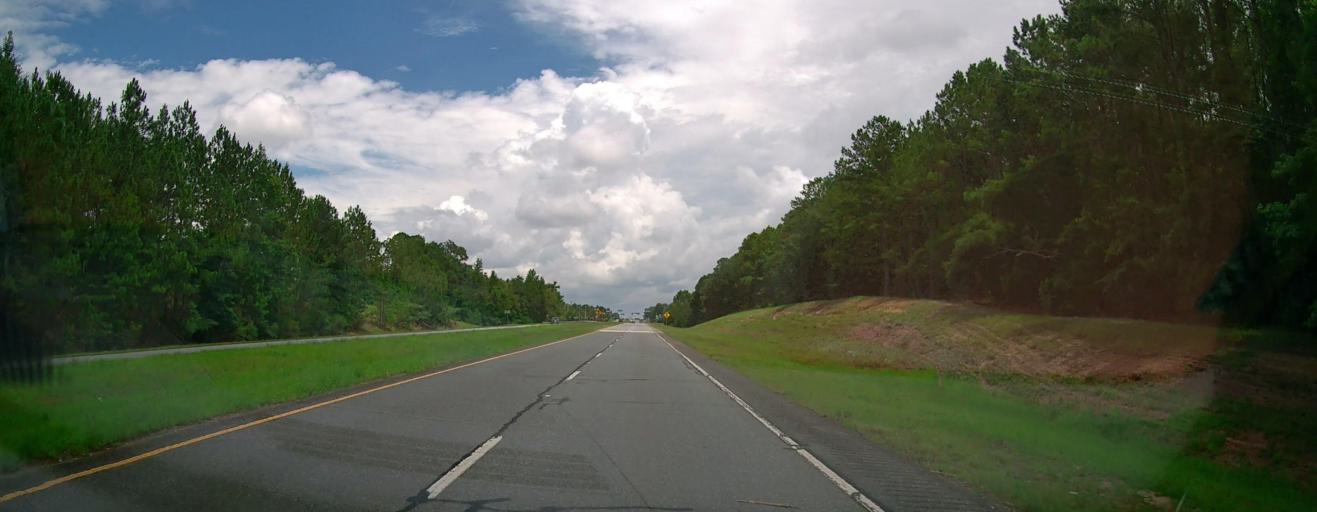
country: US
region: Georgia
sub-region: Dodge County
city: Eastman
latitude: 32.1786
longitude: -83.1869
